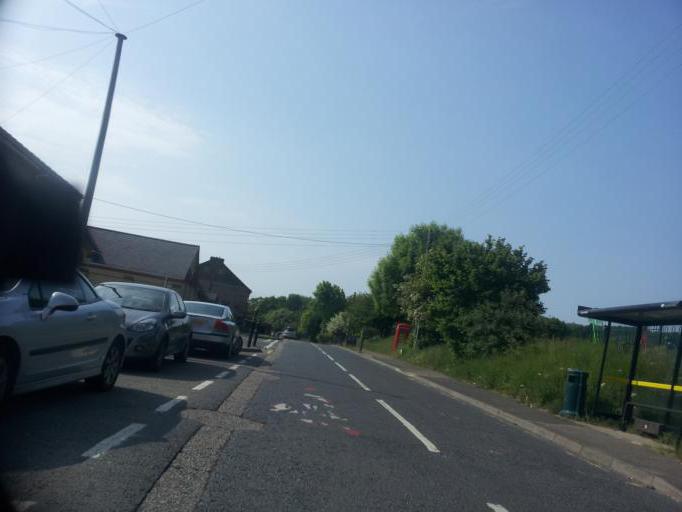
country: GB
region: England
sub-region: Kent
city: Aylesford
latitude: 51.3297
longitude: 0.4831
